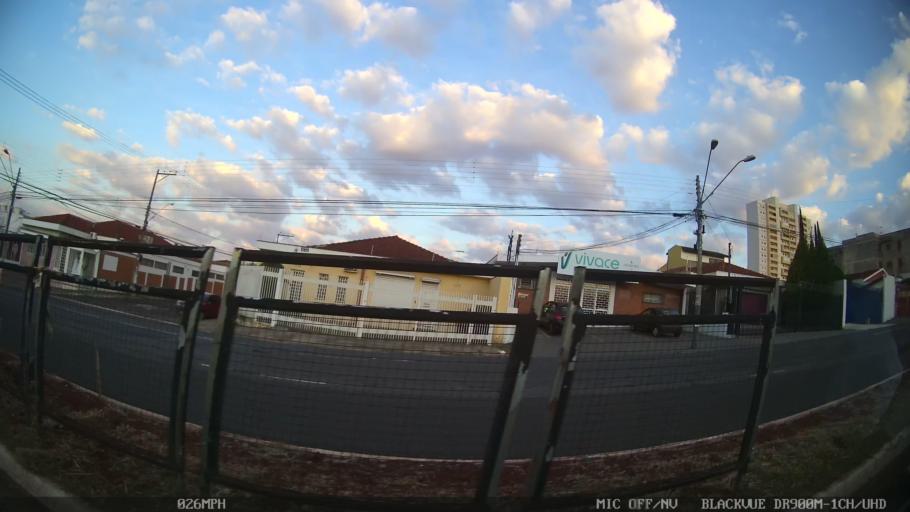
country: BR
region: Sao Paulo
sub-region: Ribeirao Preto
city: Ribeirao Preto
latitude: -21.1721
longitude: -47.7937
